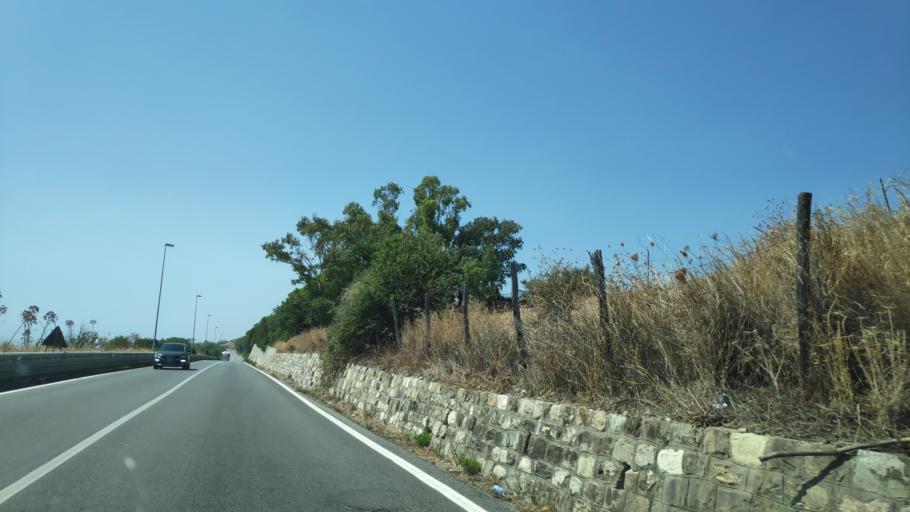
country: IT
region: Calabria
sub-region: Provincia di Reggio Calabria
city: Africo Nuovo
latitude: 38.0124
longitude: 16.1316
